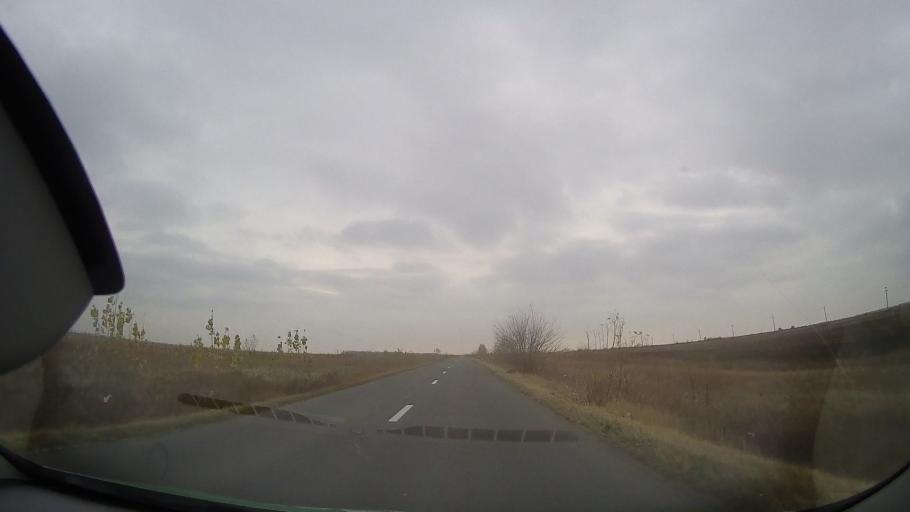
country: RO
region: Ialomita
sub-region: Comuna Garbovi
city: Garbovi
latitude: 44.7526
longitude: 26.7229
